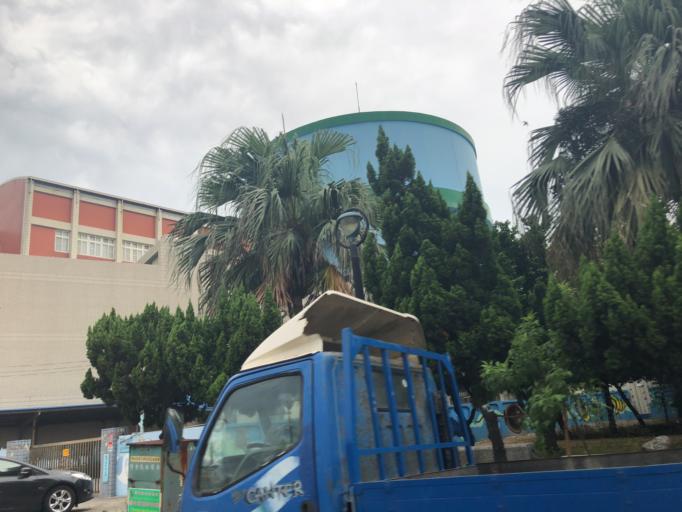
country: TW
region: Taiwan
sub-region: Chiayi
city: Taibao
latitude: 23.7015
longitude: 120.1999
